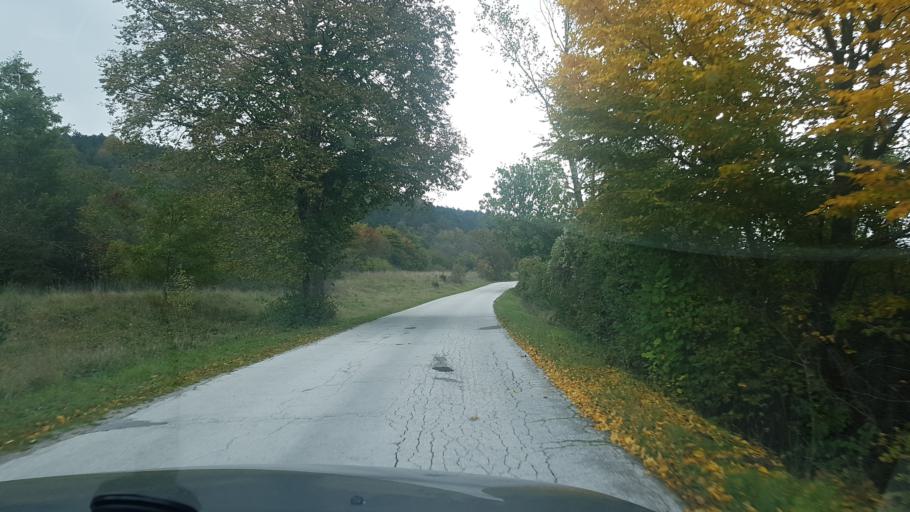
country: HR
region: Istarska
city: Buzet
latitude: 45.5032
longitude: 13.9909
